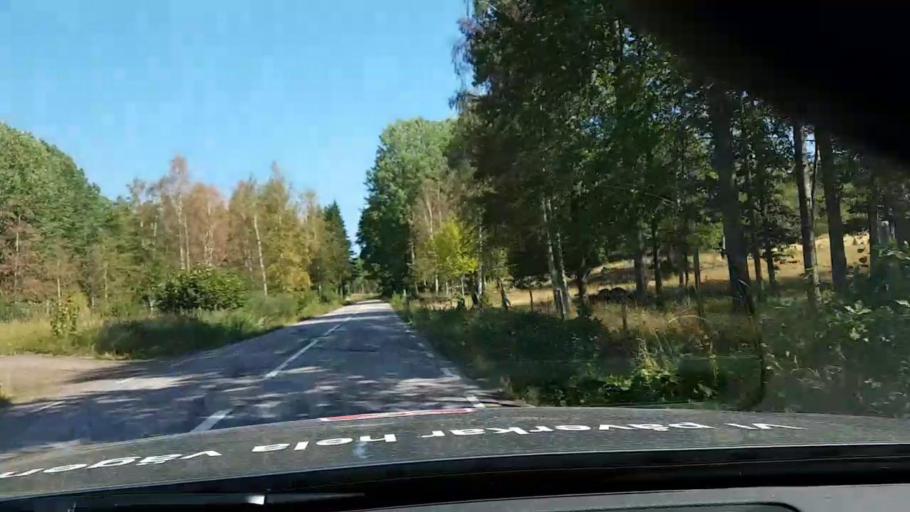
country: SE
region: Kalmar
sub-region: Hultsfreds Kommun
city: Virserum
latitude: 57.1310
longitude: 15.6573
